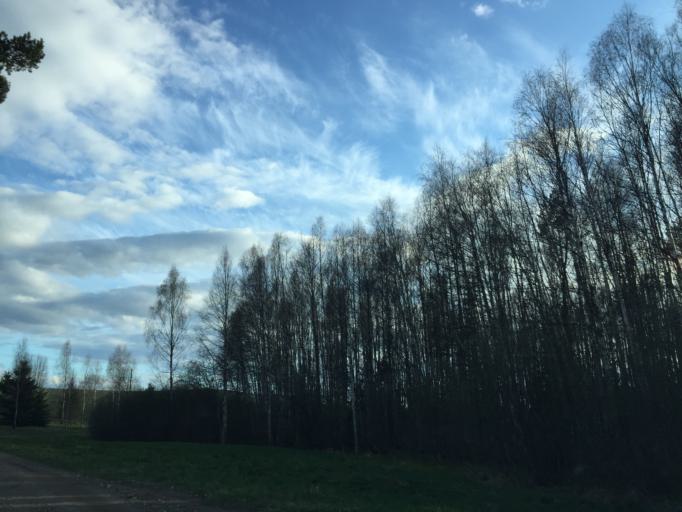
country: LV
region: Rezekne
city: Rezekne
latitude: 56.5827
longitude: 27.3427
